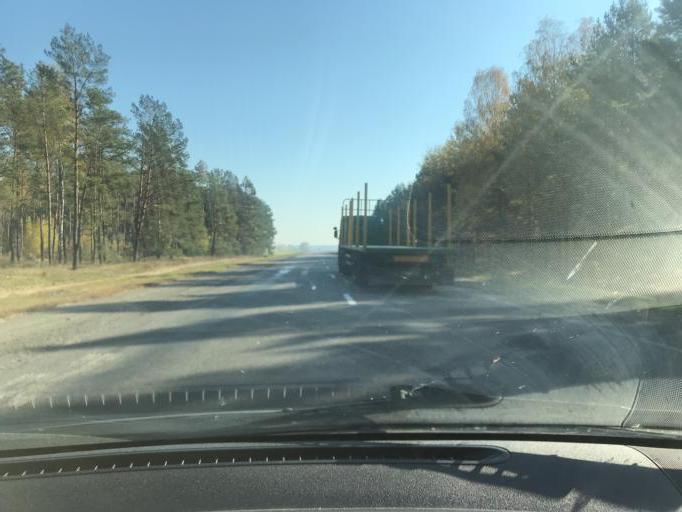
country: BY
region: Brest
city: Luninyets
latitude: 52.2583
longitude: 27.0386
